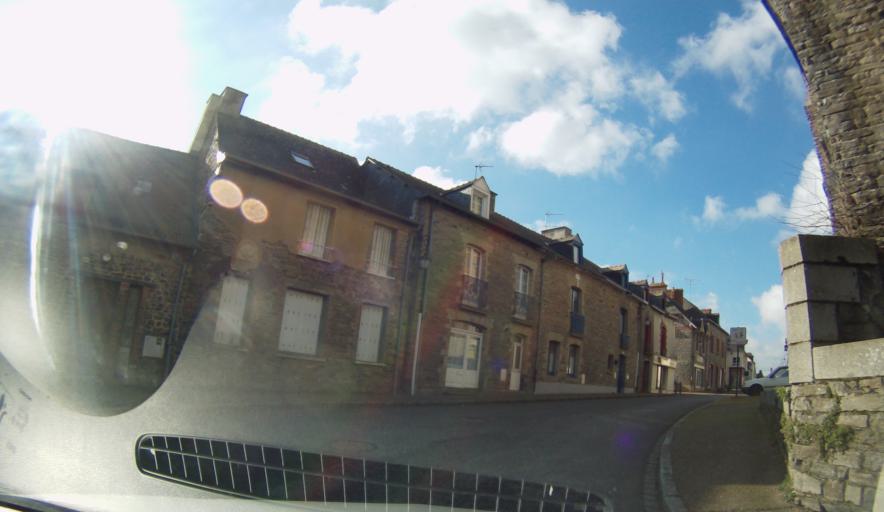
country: FR
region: Brittany
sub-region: Departement d'Ille-et-Vilaine
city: Corps-Nuds
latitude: 47.9777
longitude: -1.5873
